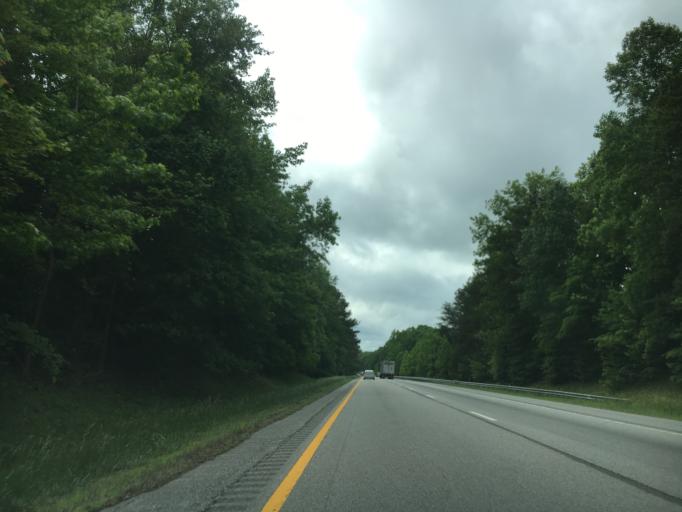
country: US
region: Virginia
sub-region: Mecklenburg County
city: South Hill
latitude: 36.7696
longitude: -78.0564
